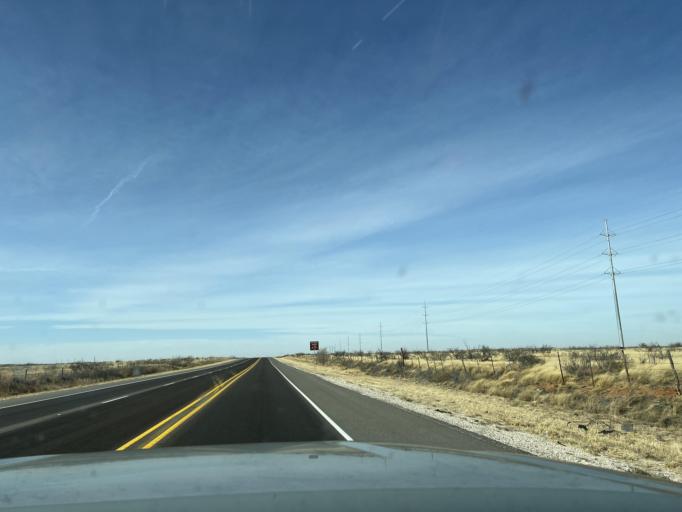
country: US
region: Texas
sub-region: Andrews County
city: Andrews
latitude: 32.3545
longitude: -102.7558
